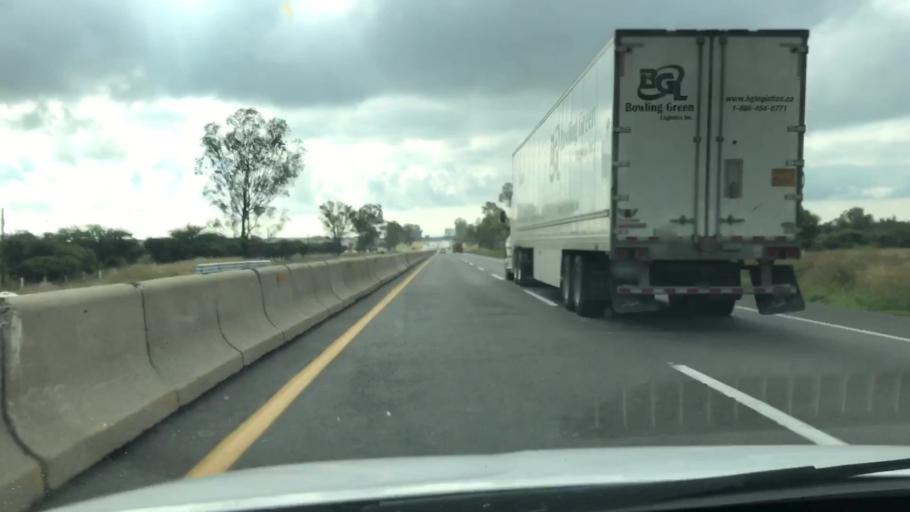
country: MX
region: Guanajuato
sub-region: Leon
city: Centro Familiar la Soledad
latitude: 21.0950
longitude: -101.7740
